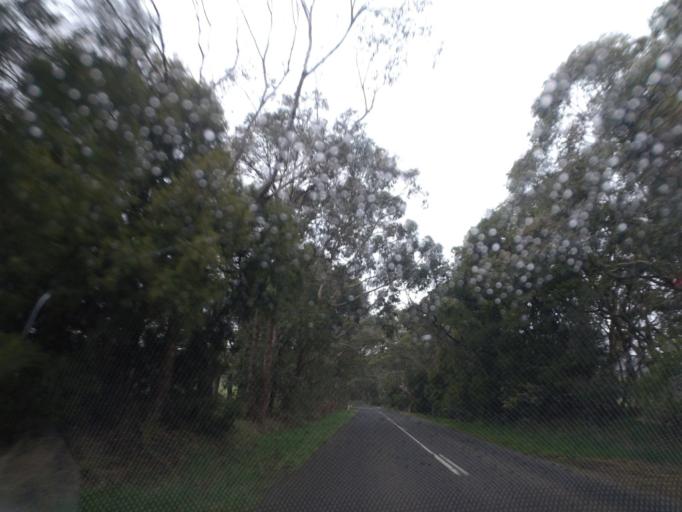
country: AU
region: Victoria
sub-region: Hume
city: Sunbury
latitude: -37.3522
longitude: 144.6470
